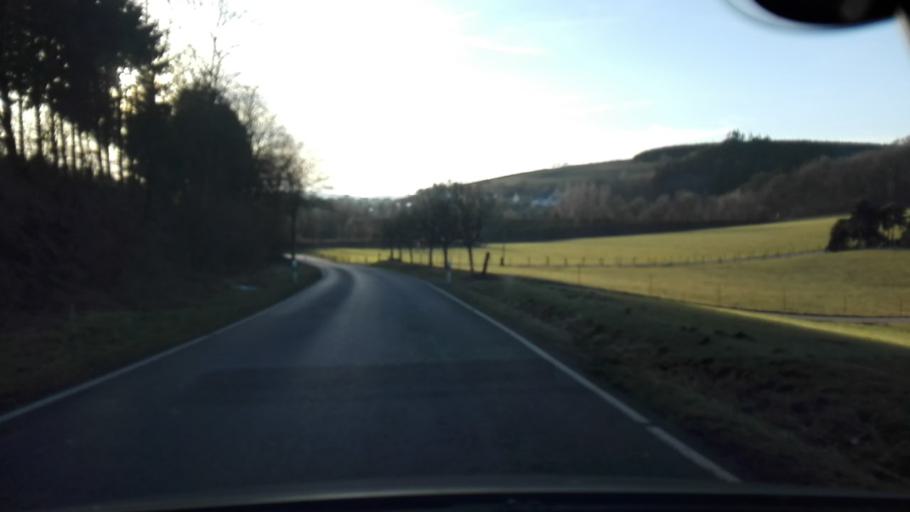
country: DE
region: North Rhine-Westphalia
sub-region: Regierungsbezirk Arnsberg
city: Lennestadt
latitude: 51.1957
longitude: 8.0619
